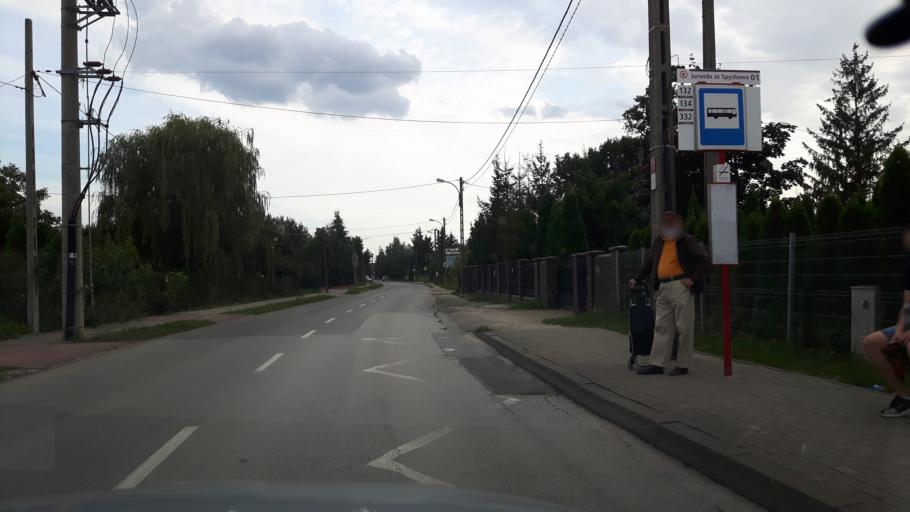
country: PL
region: Masovian Voivodeship
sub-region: Warszawa
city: Targowek
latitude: 52.3173
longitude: 21.0506
